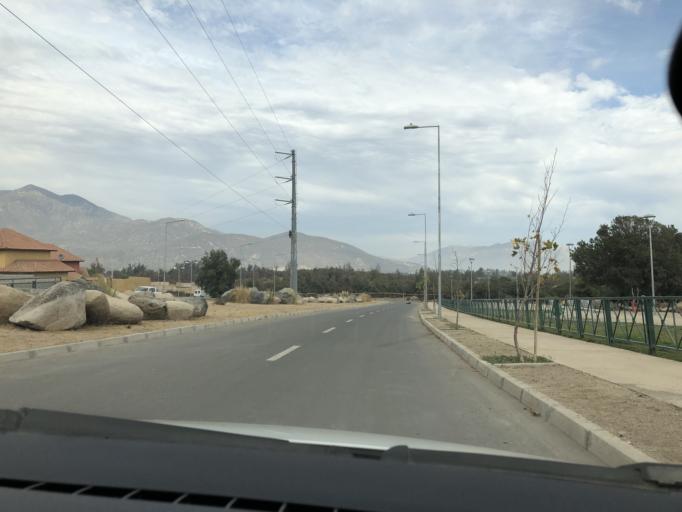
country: CL
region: Santiago Metropolitan
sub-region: Provincia de Cordillera
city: Puente Alto
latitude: -33.5838
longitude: -70.5168
